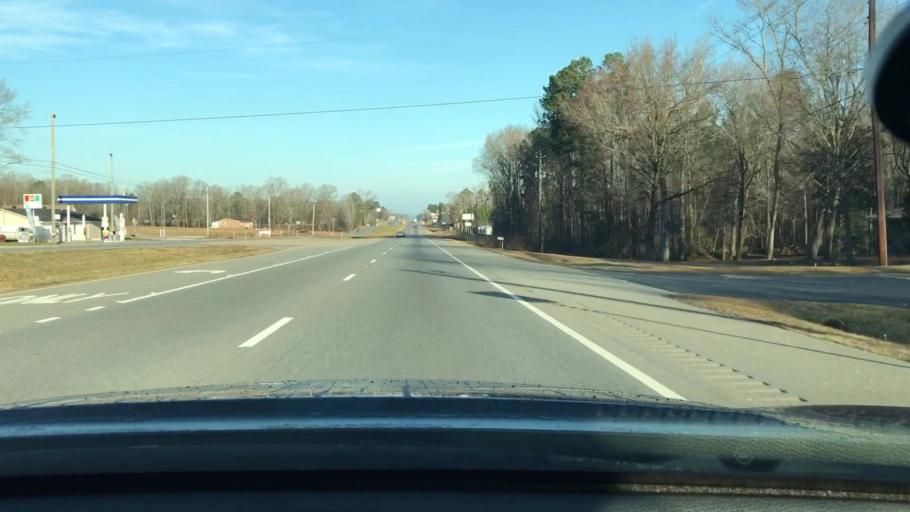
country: US
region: Alabama
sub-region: Talladega County
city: Mignon
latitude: 33.2145
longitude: -86.3148
